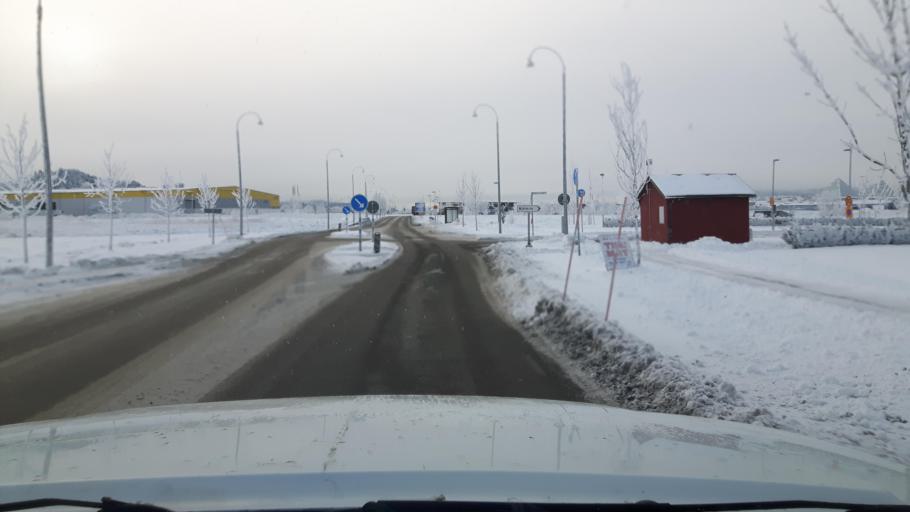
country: SE
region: Halland
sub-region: Kungsbacka Kommun
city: Kungsbacka
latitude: 57.5173
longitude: 12.0812
